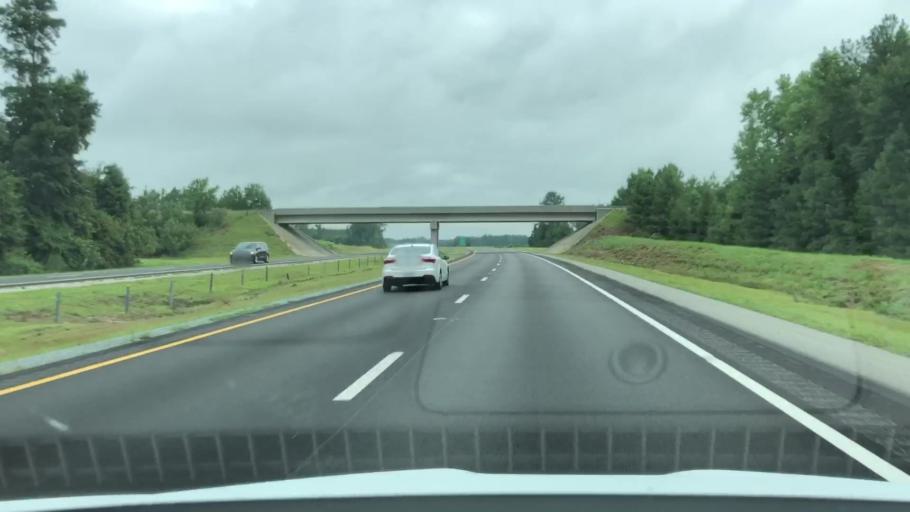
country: US
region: North Carolina
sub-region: Wayne County
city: Fremont
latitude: 35.5266
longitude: -77.9888
